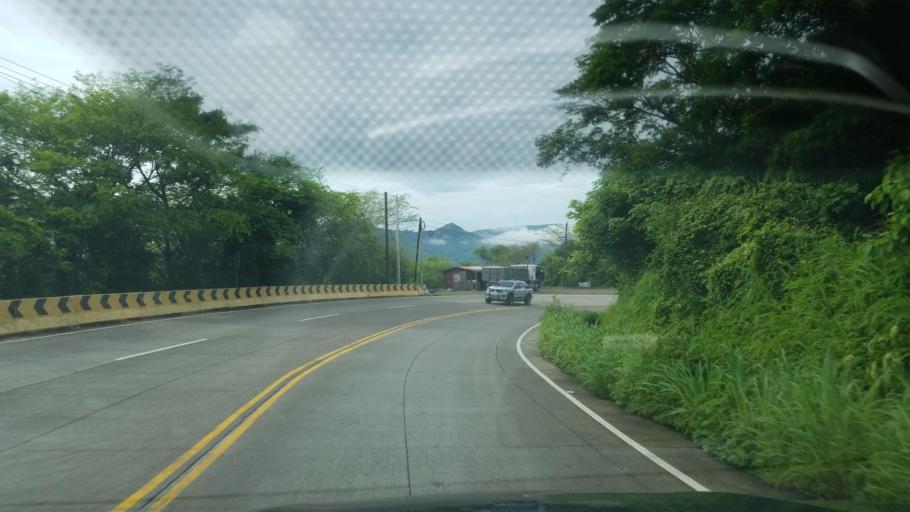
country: HN
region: Francisco Morazan
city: El Porvenir
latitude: 13.7013
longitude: -87.3160
